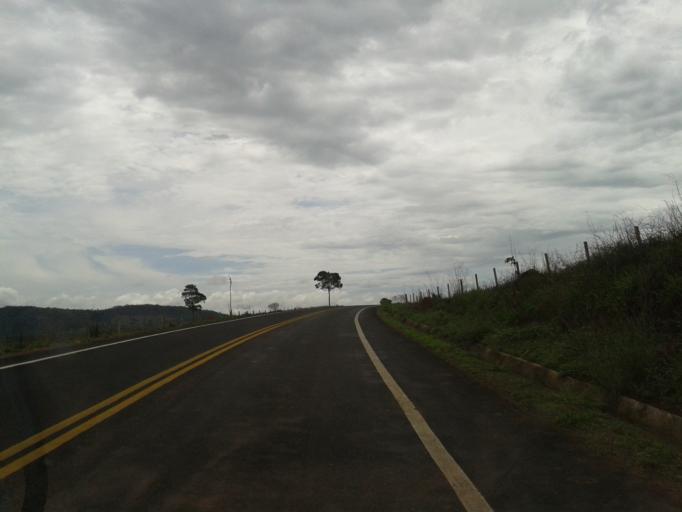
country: BR
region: Goias
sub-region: Buriti Alegre
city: Buriti Alegre
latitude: -18.1467
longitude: -48.8654
